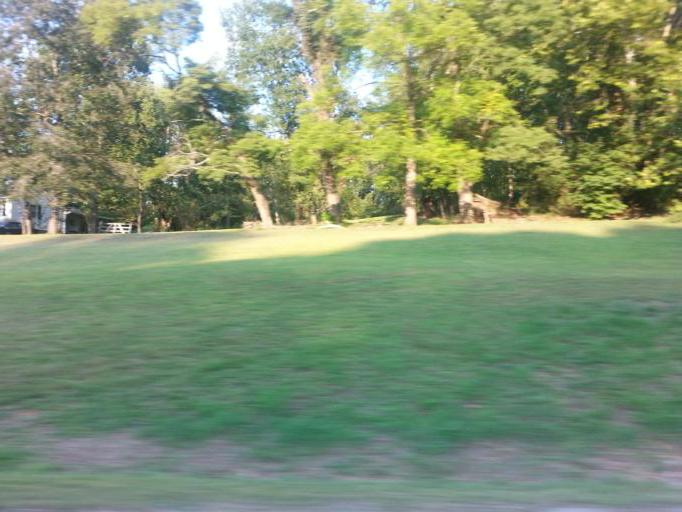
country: US
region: Tennessee
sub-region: Knox County
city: Mascot
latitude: 36.0816
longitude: -83.7438
